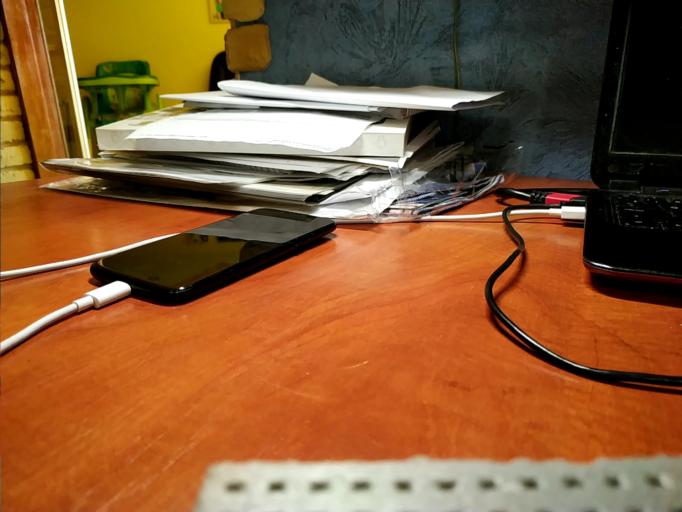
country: RU
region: Tverskaya
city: Kalashnikovo
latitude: 57.3980
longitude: 35.2457
